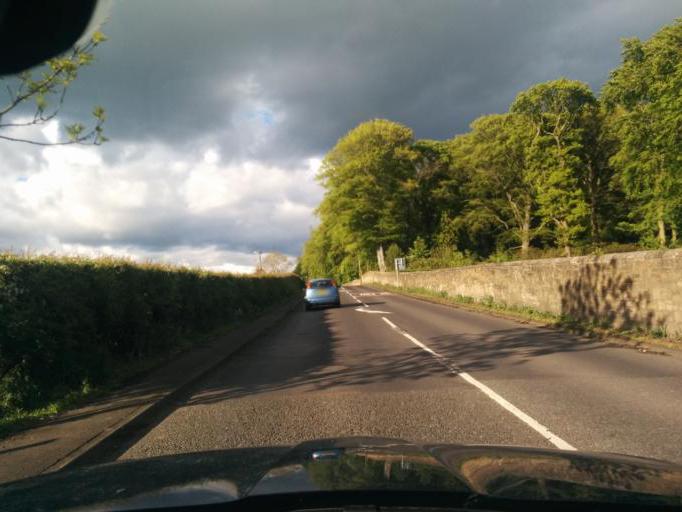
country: GB
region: England
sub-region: Northumberland
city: Bedlington
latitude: 55.1148
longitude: -1.6232
